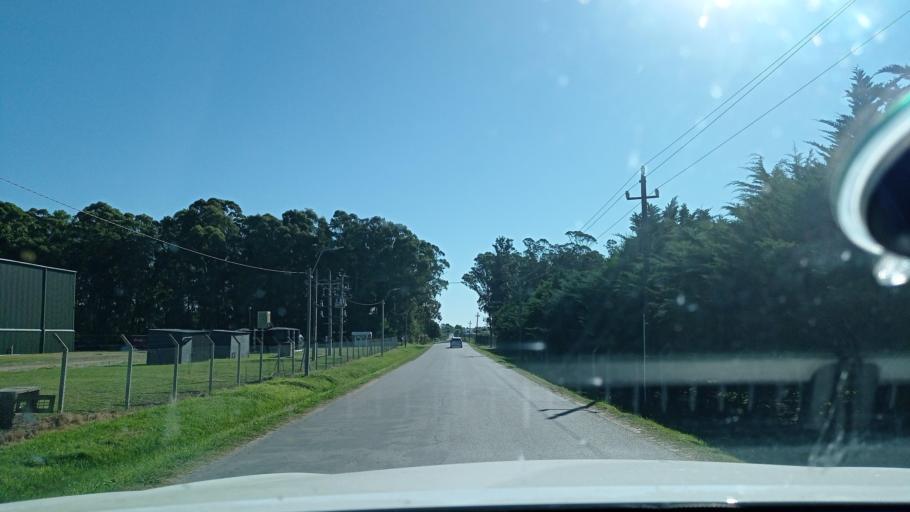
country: UY
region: Canelones
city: Pando
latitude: -34.7580
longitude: -55.9827
